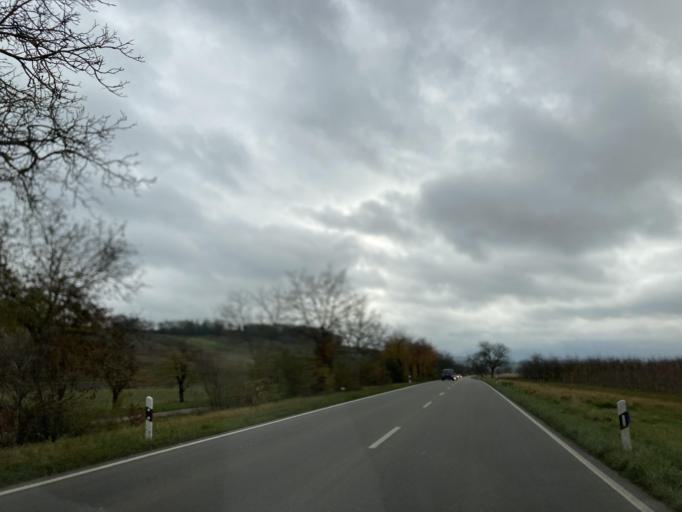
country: DE
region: Baden-Wuerttemberg
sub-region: Freiburg Region
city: Auggen
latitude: 47.7817
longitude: 7.5868
